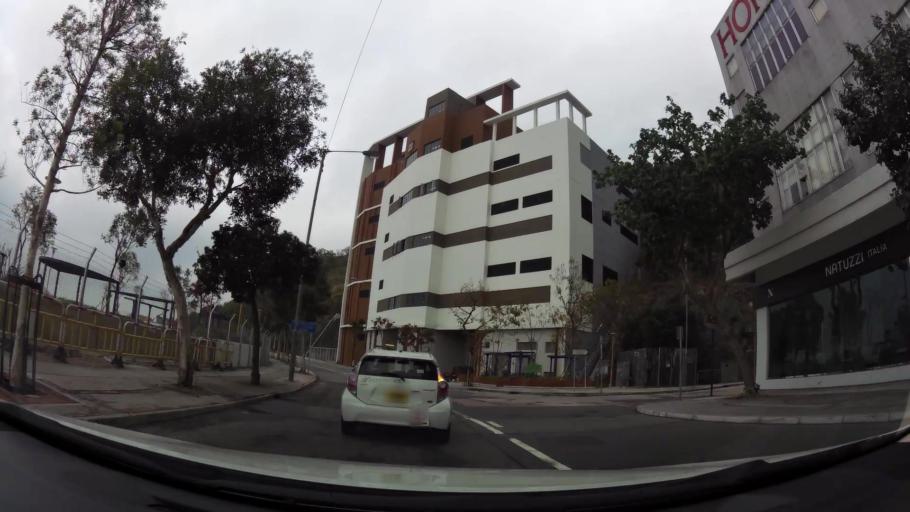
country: HK
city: Sok Kwu Wan
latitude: 22.2390
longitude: 114.1519
